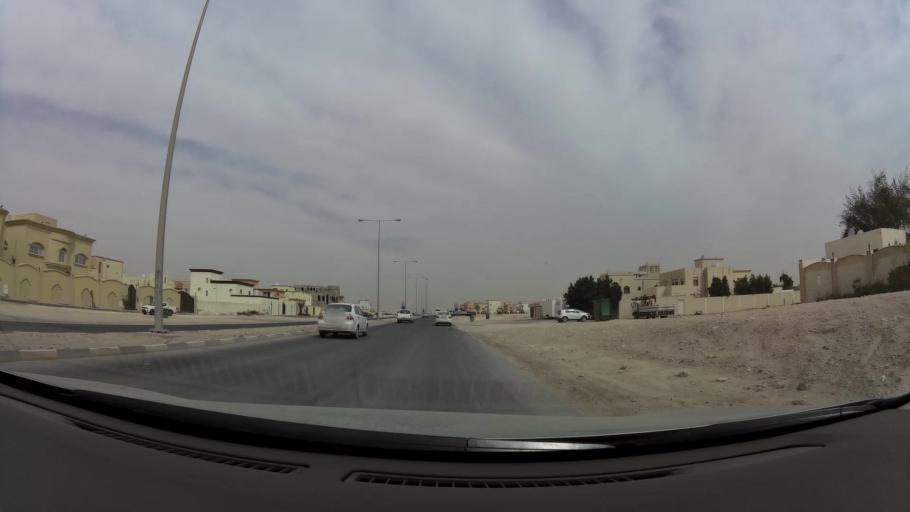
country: QA
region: Baladiyat ad Dawhah
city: Doha
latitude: 25.2103
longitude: 51.4832
